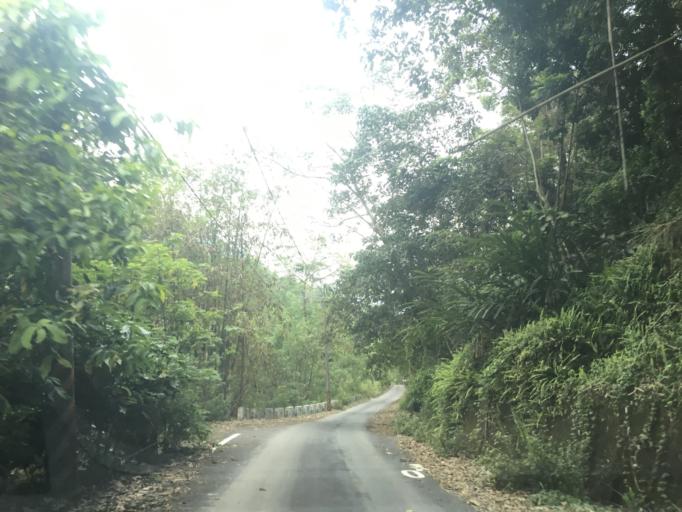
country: TW
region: Taiwan
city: Zhongxing New Village
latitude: 24.0449
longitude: 120.8078
